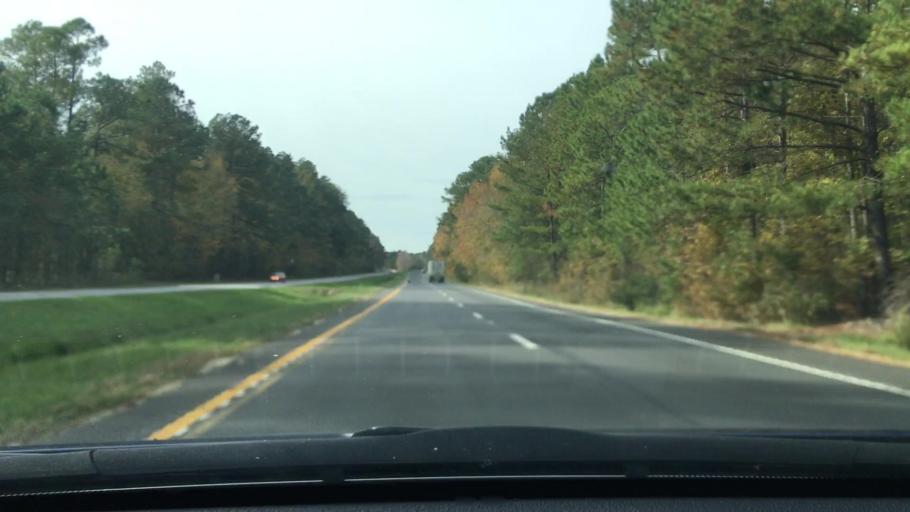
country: US
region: South Carolina
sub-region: Sumter County
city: Stateburg
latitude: 33.9505
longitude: -80.5542
